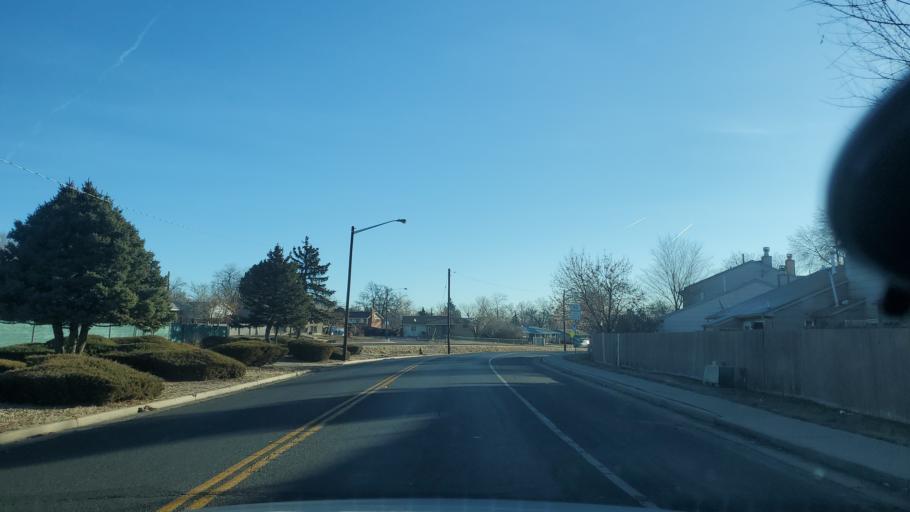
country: US
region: Colorado
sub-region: Adams County
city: Welby
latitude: 39.8465
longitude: -104.9768
